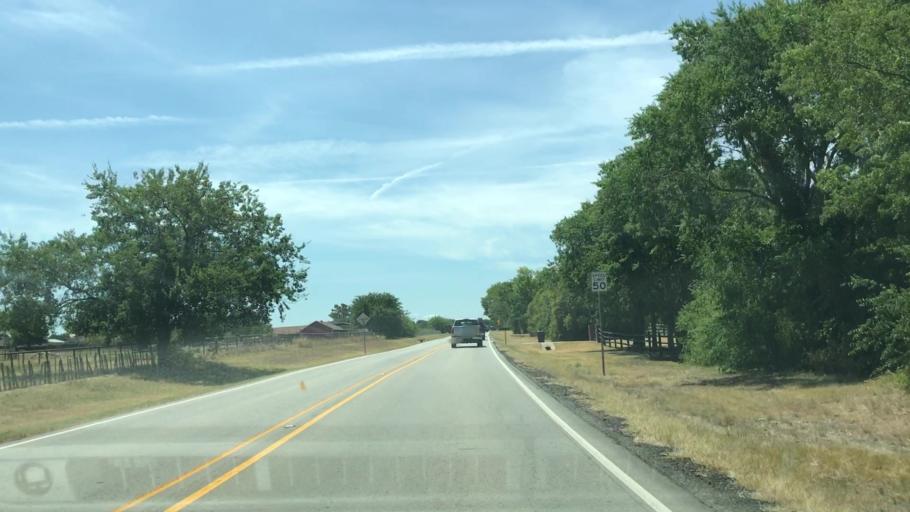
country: US
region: Texas
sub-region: Collin County
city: Lucas
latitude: 33.0989
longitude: -96.5937
